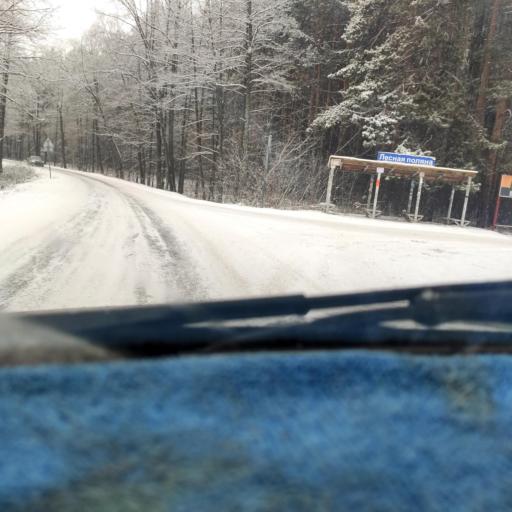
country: RU
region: Bashkortostan
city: Avdon
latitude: 54.6750
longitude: 55.8453
